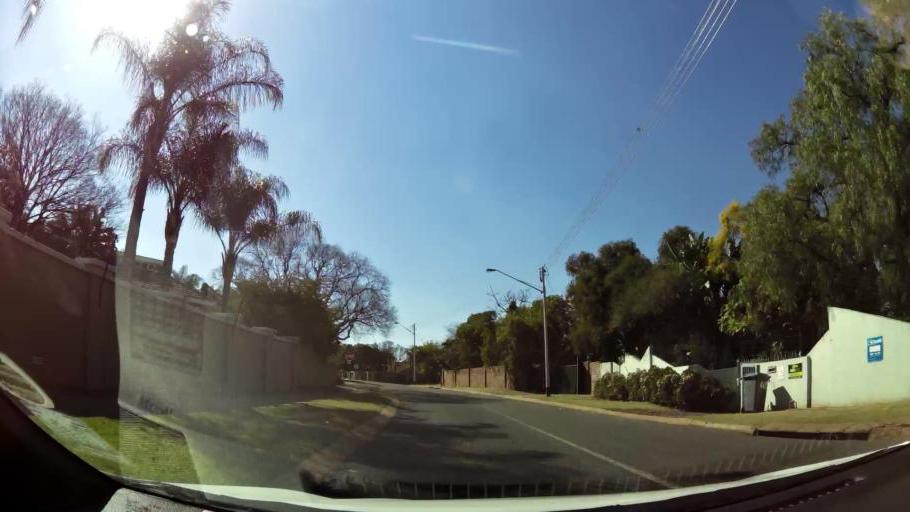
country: ZA
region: Gauteng
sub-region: City of Tshwane Metropolitan Municipality
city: Pretoria
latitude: -25.7598
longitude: 28.2712
